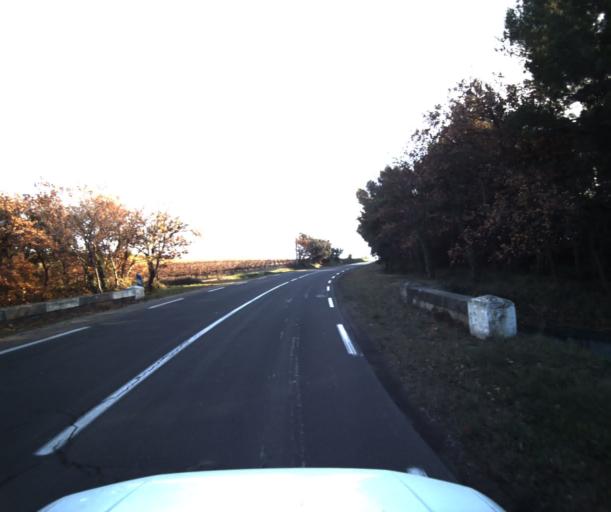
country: FR
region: Provence-Alpes-Cote d'Azur
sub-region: Departement du Vaucluse
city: Villelaure
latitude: 43.7006
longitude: 5.4604
